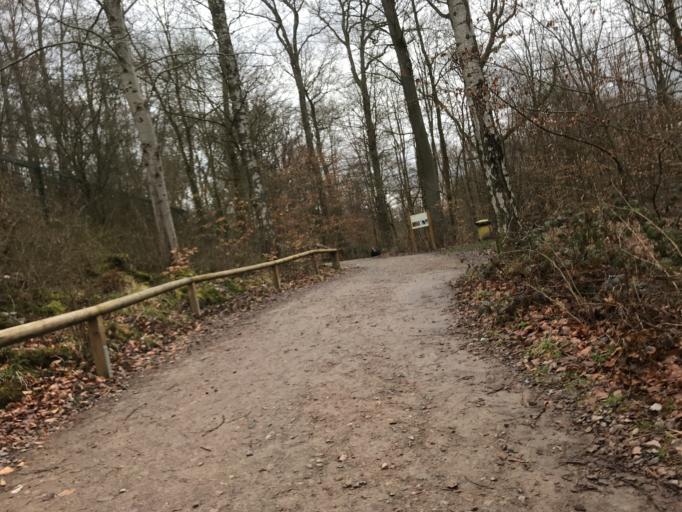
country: DE
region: Hesse
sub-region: Regierungsbezirk Darmstadt
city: Wiesbaden
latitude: 50.1066
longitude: 8.1948
